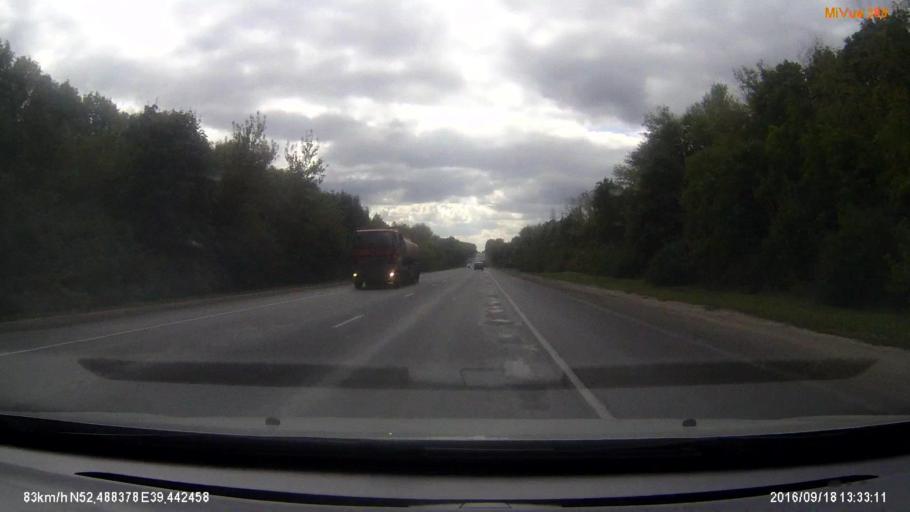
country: RU
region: Lipetsk
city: Borinskoye
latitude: 52.4754
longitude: 39.4263
